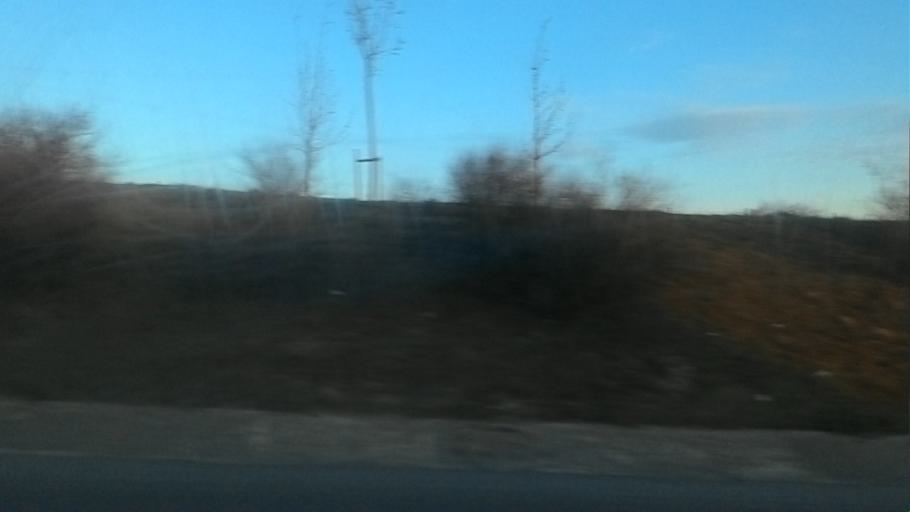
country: TR
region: Istanbul
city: Selimpasa
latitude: 41.0651
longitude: 28.3800
